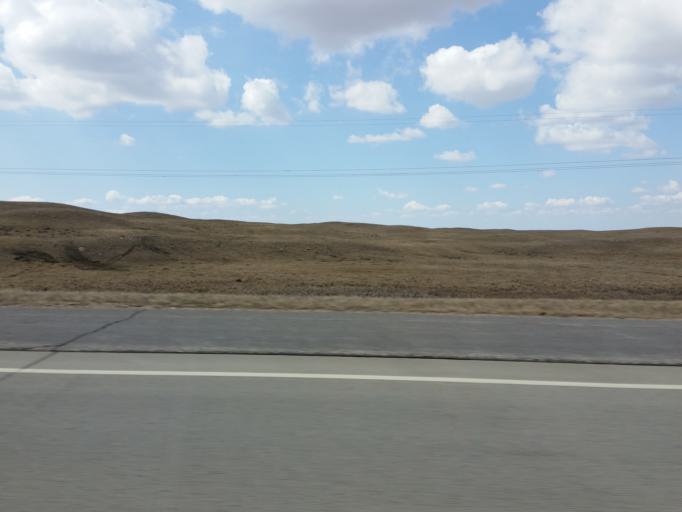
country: US
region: South Dakota
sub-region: Roberts County
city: Sisseton
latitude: 45.3741
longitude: -97.0497
